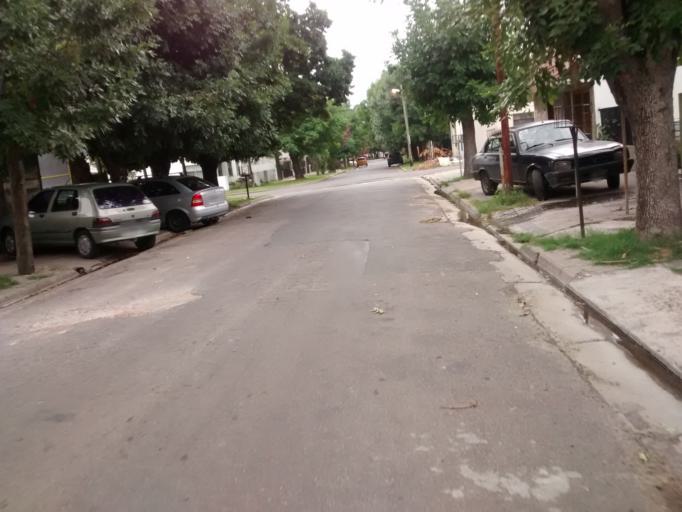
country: AR
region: Buenos Aires
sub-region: Partido de La Plata
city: La Plata
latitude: -34.9381
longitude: -57.9224
